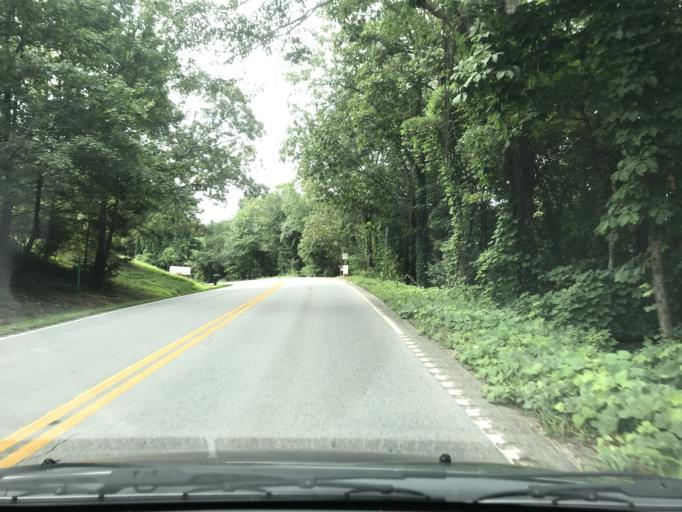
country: US
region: Tennessee
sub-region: Hamilton County
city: Lakesite
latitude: 35.1937
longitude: -85.0698
